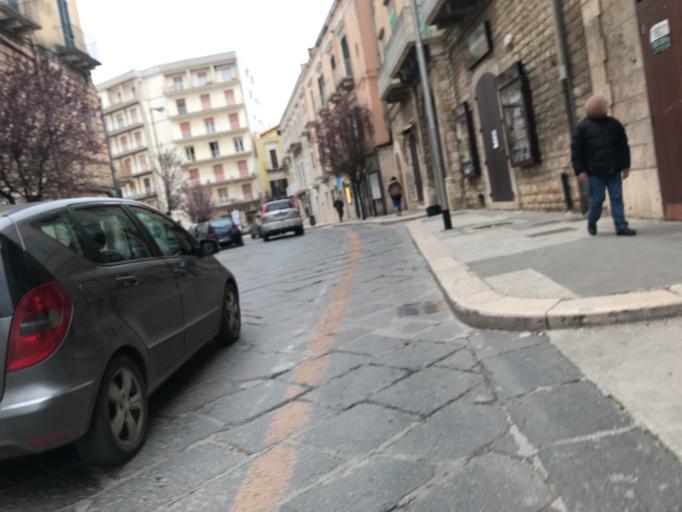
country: IT
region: Apulia
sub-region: Provincia di Bari
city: Corato
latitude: 41.1532
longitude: 16.4092
